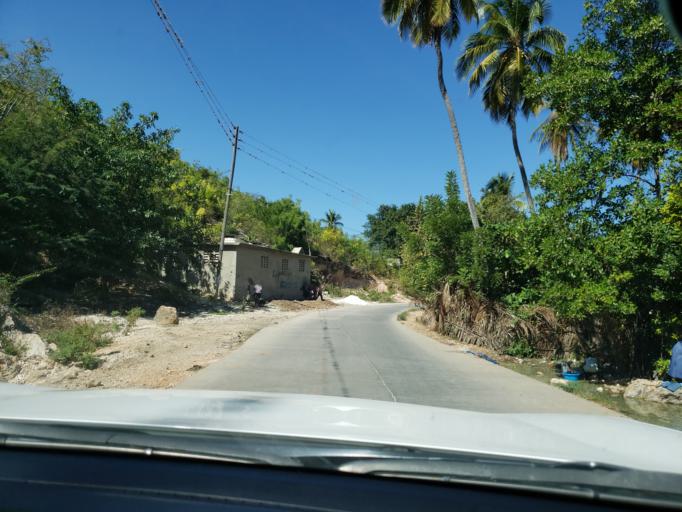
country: HT
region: Nippes
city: Miragoane
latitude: 18.4455
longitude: -73.1050
